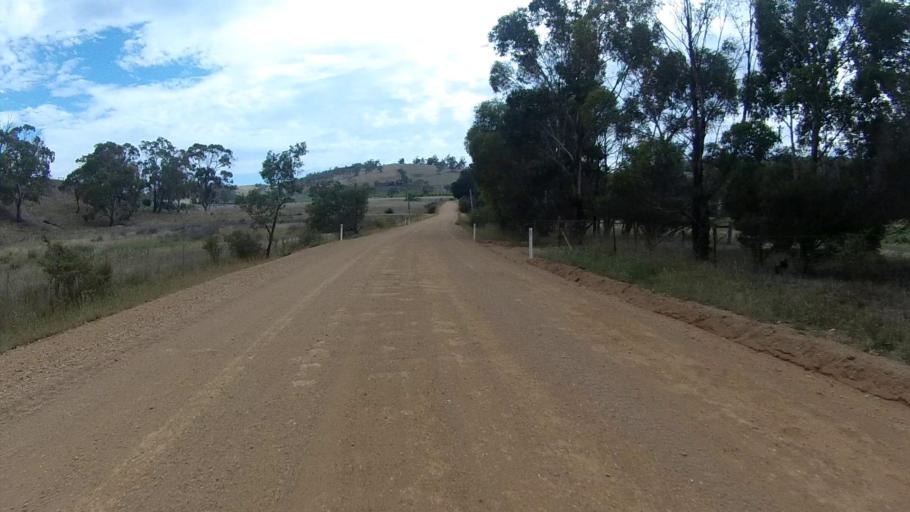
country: AU
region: Tasmania
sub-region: Sorell
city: Sorell
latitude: -42.6955
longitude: 147.4633
